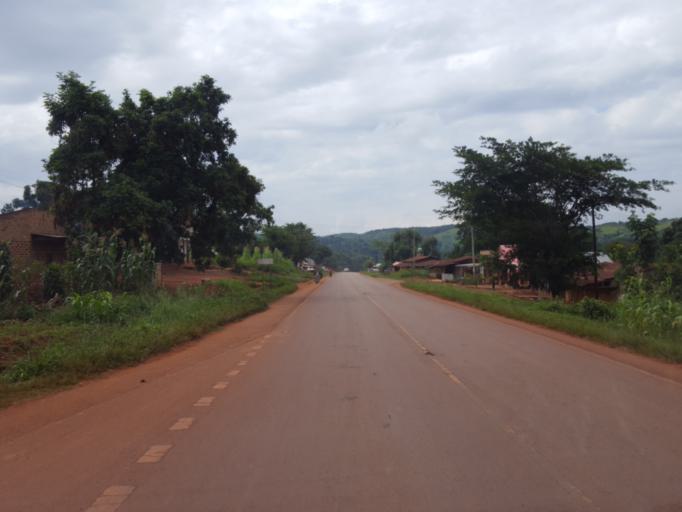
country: UG
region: Central Region
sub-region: Mityana District
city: Mityana
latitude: 0.6341
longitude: 32.1102
